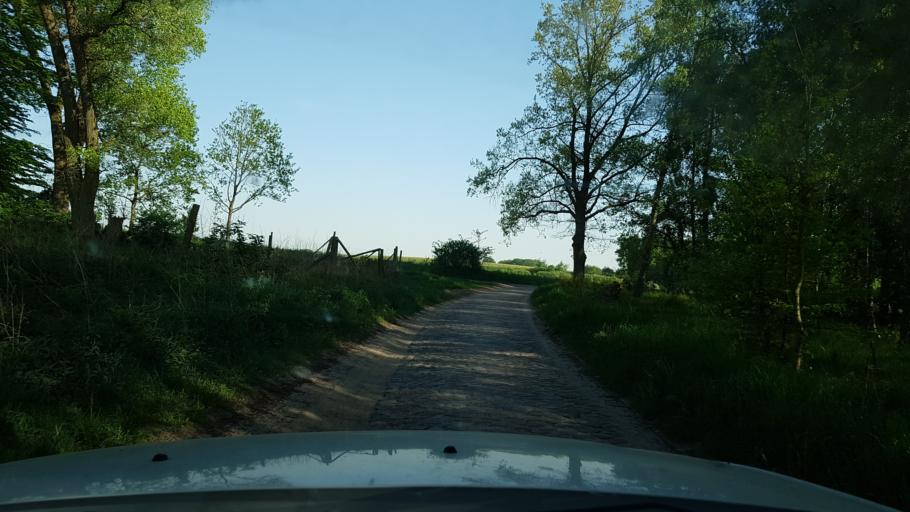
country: PL
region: West Pomeranian Voivodeship
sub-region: Powiat lobeski
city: Resko
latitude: 53.7150
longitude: 15.3377
